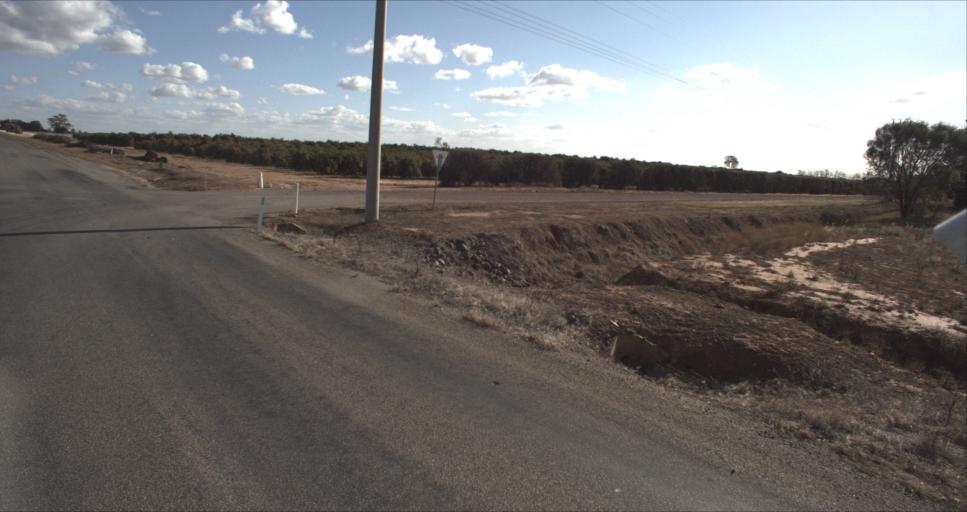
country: AU
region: New South Wales
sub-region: Leeton
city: Leeton
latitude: -34.5277
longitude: 146.2821
